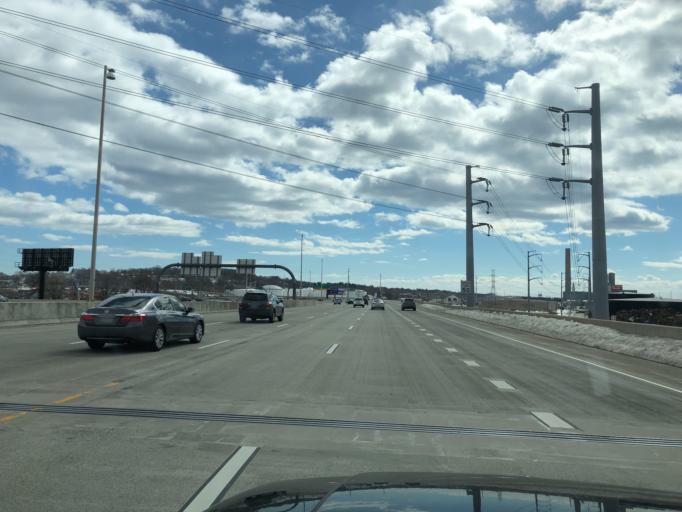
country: US
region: Connecticut
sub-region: New Haven County
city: New Haven
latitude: 41.2955
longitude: -72.9020
